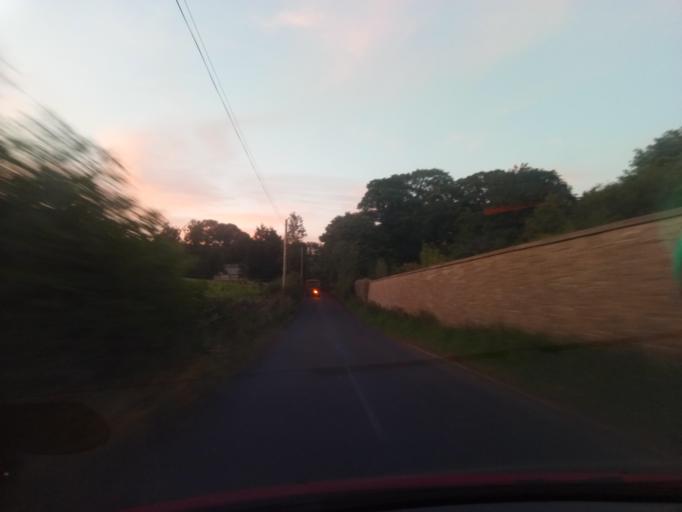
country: GB
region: England
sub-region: Northumberland
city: Warden
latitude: 54.9867
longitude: -2.2231
